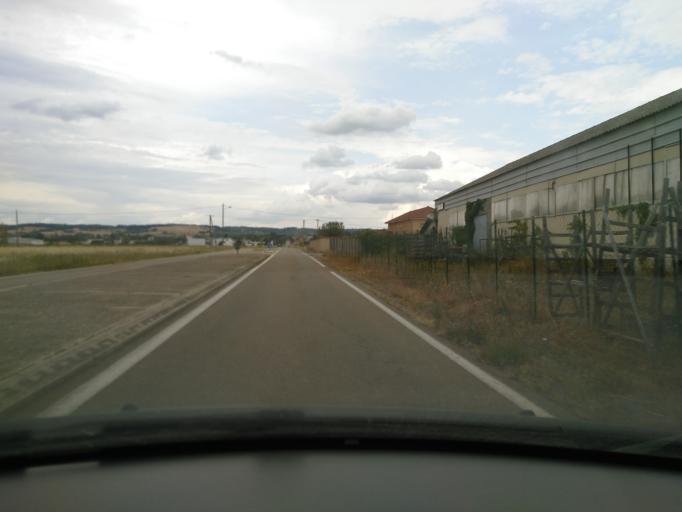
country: FR
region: Rhone-Alpes
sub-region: Departement de l'Isere
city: Beaurepaire
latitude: 45.3683
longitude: 5.0279
